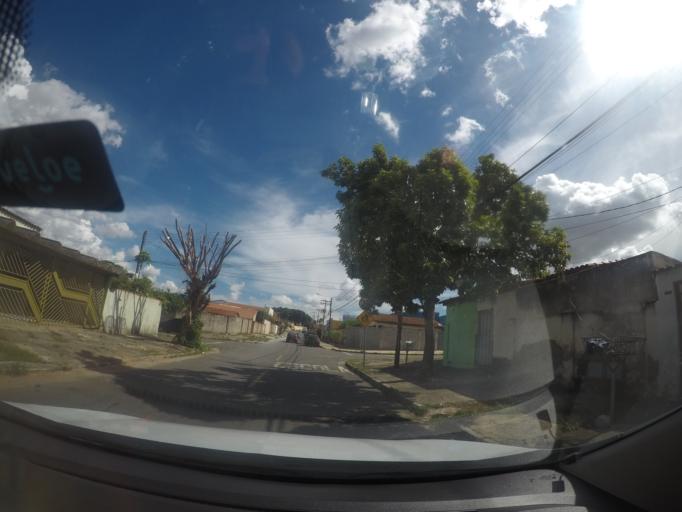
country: BR
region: Goias
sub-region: Goiania
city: Goiania
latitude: -16.6790
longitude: -49.3047
